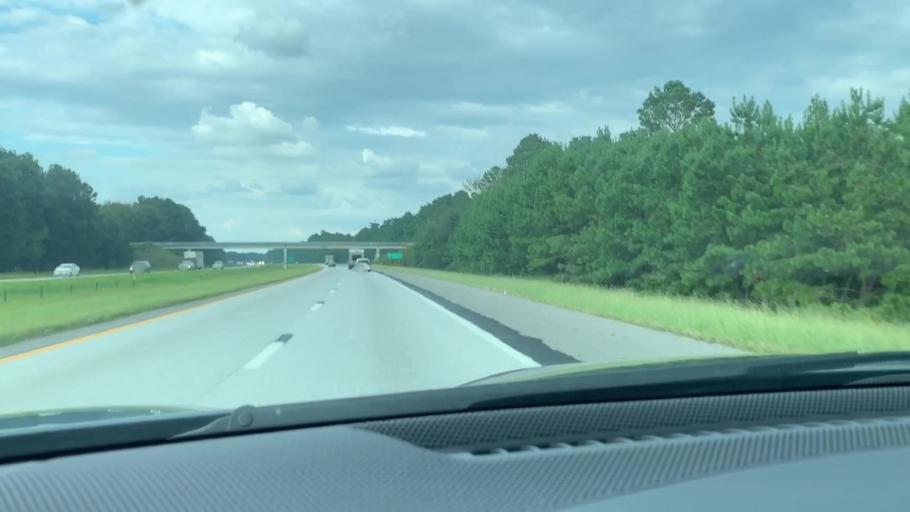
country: US
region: South Carolina
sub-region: Dorchester County
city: Saint George
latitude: 33.2933
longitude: -80.5583
